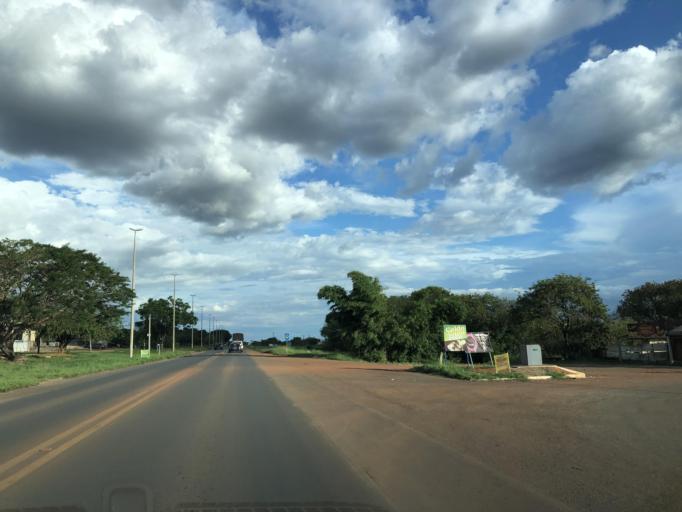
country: BR
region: Goias
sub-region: Luziania
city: Luziania
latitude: -16.0333
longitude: -48.0744
